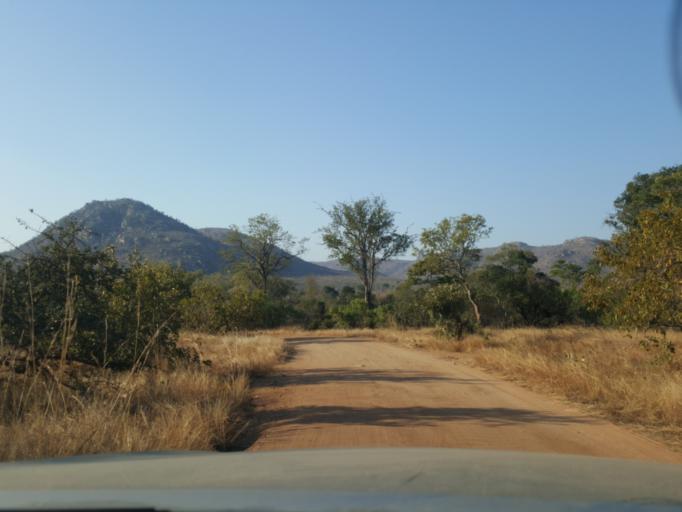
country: SZ
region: Hhohho
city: Ntfonjeni
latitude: -25.4239
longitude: 31.4422
